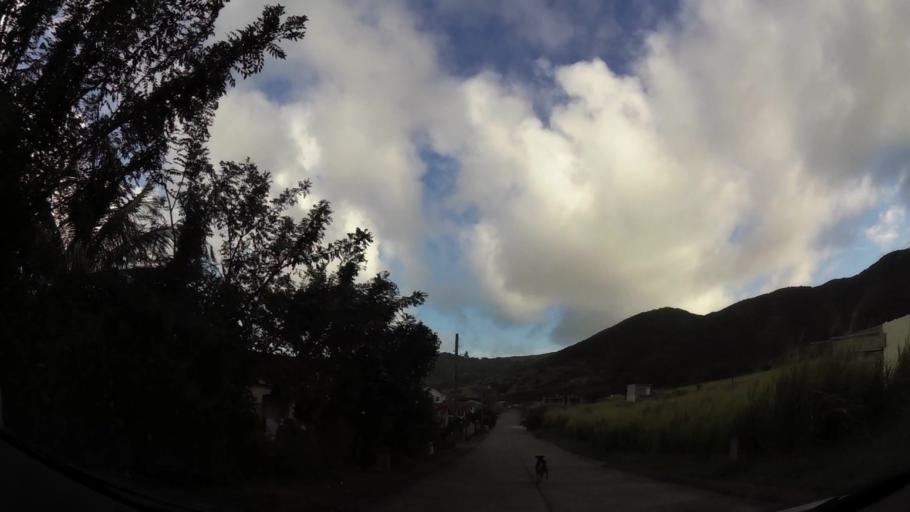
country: KN
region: Saint Mary Cayon
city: Cayon
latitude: 17.3477
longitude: -62.7305
